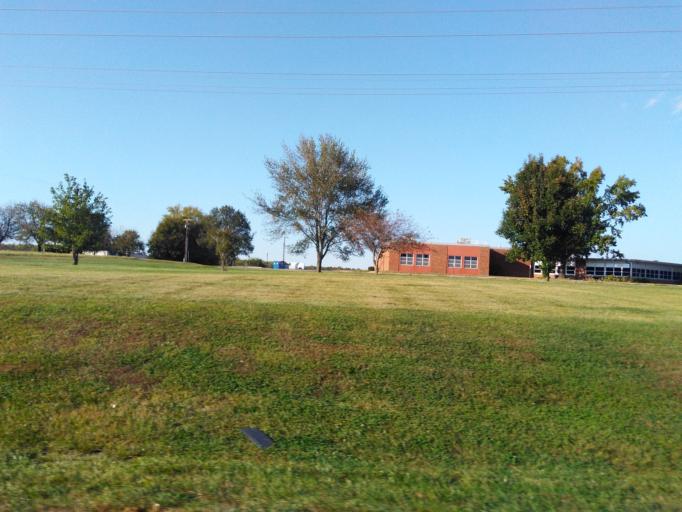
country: US
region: Illinois
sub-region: Madison County
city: Saint Jacob
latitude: 38.7161
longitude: -89.8213
